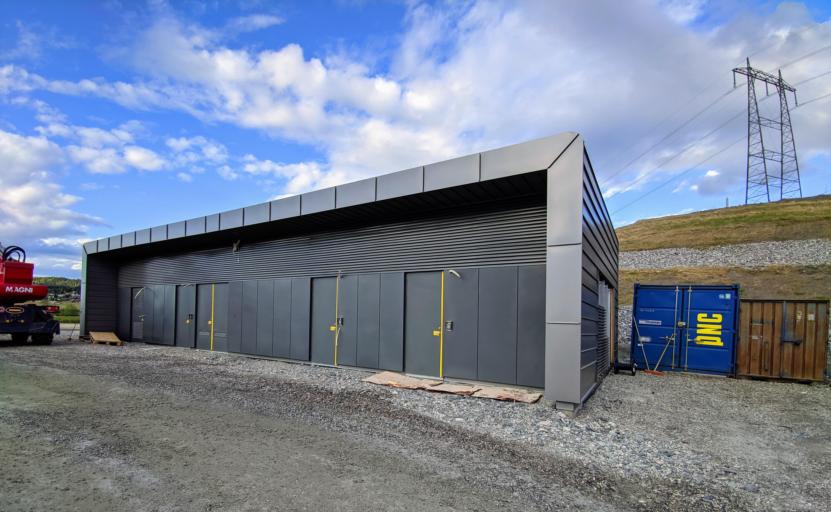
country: NO
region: Akershus
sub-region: Eidsvoll
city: Eidsvoll
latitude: 60.3913
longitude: 11.2383
